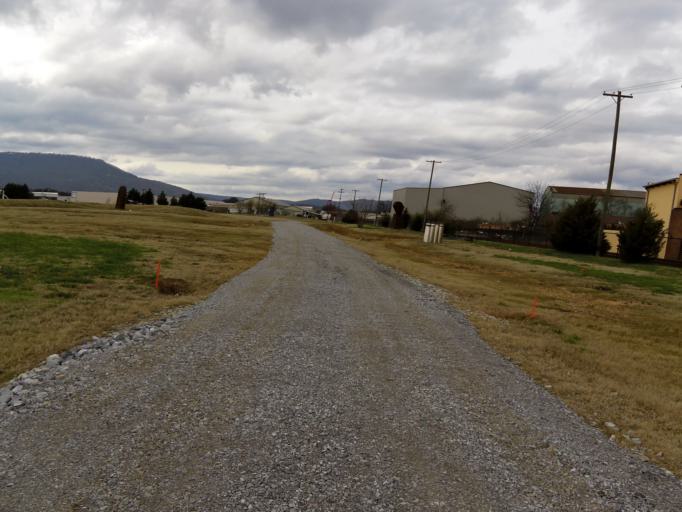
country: US
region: Tennessee
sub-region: Hamilton County
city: Chattanooga
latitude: 35.0282
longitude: -85.2923
